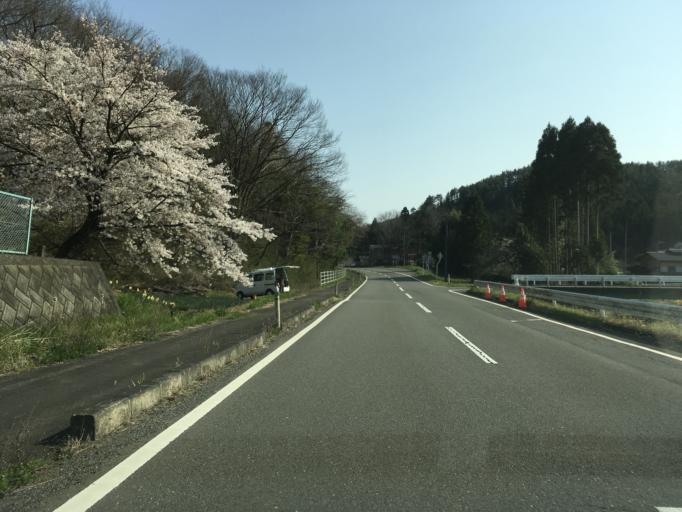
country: JP
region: Iwate
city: Ichinoseki
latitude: 38.7927
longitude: 141.3220
